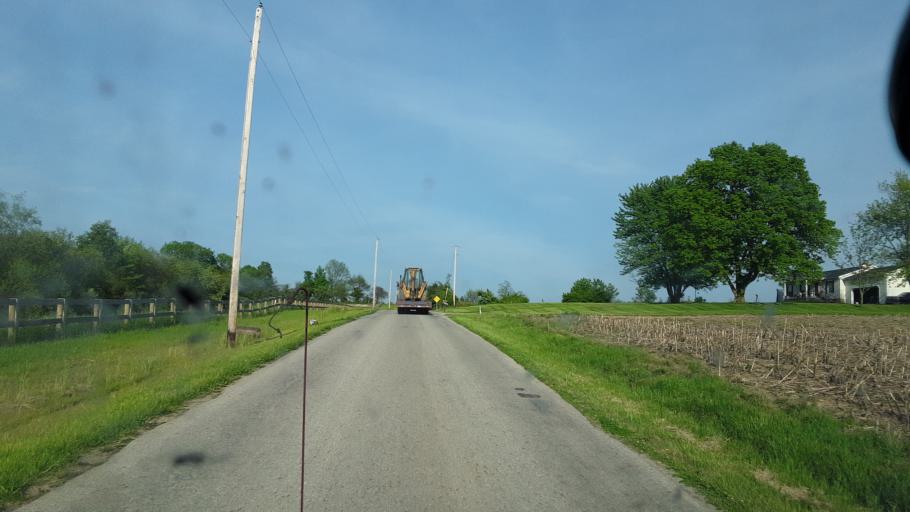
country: US
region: Ohio
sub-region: Ross County
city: Kingston
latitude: 39.5122
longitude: -82.7574
